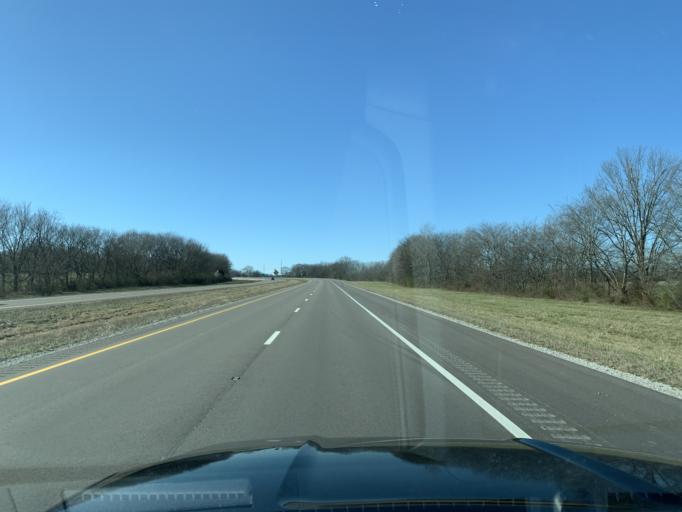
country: US
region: Tennessee
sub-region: Maury County
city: Mount Pleasant
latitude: 35.5506
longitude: -87.2123
